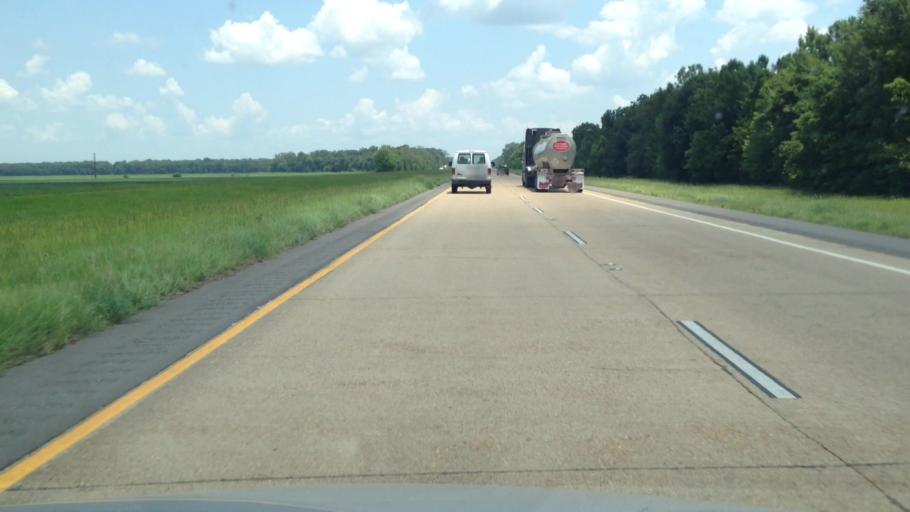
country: US
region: Louisiana
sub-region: Rapides Parish
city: Lecompte
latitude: 31.0044
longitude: -92.3505
